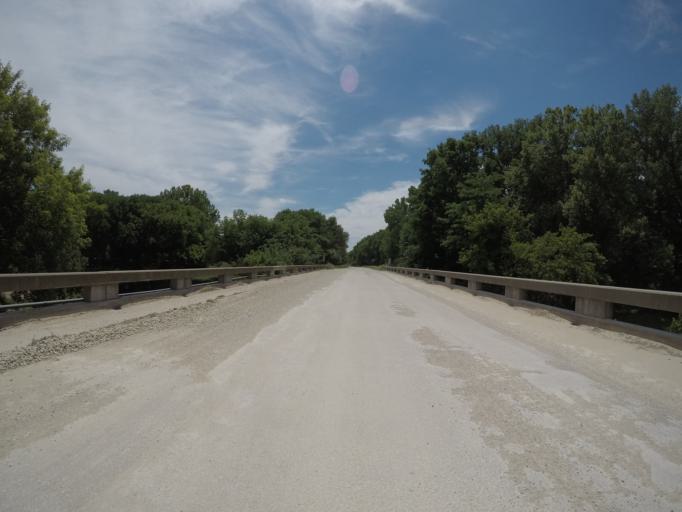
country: US
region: Kansas
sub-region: Wabaunsee County
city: Alma
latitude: 38.9589
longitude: -96.2520
